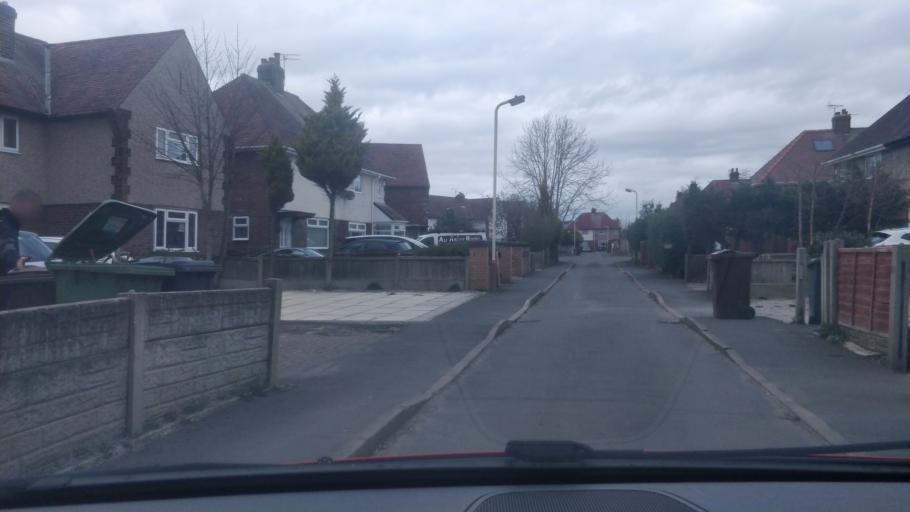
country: GB
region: England
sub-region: Sefton
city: Southport
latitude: 53.6151
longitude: -3.0158
